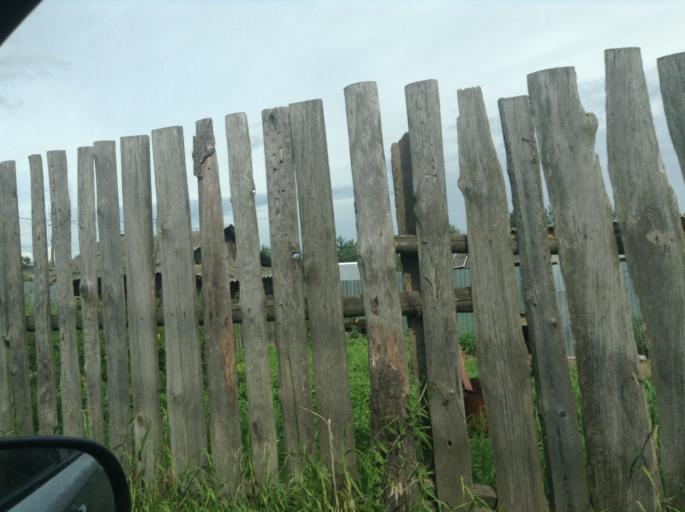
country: RU
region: Moskovskaya
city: Yegor'yevsk
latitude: 55.3640
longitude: 39.0963
